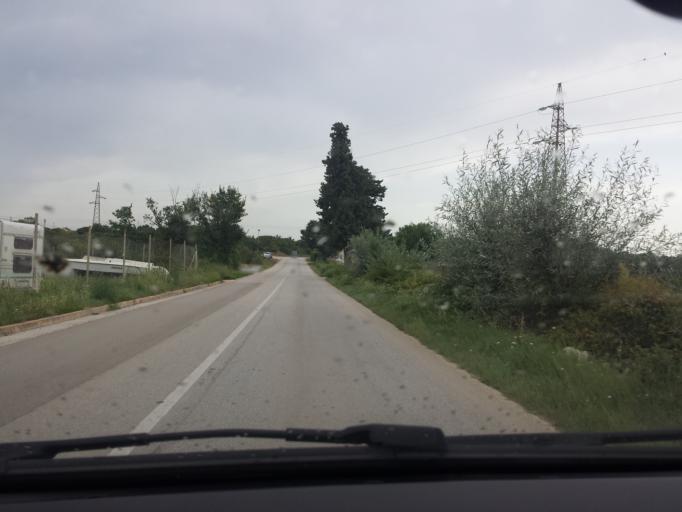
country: HR
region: Istarska
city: Galizana
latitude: 44.9072
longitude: 13.8554
